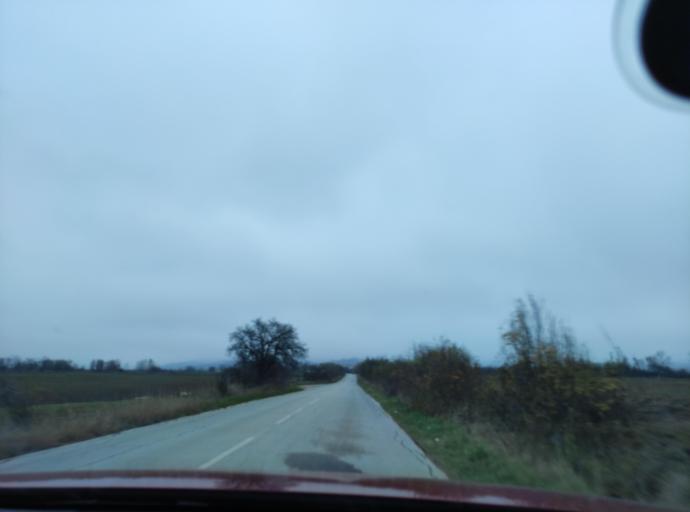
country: BG
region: Lovech
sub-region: Obshtina Yablanitsa
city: Yablanitsa
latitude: 43.0797
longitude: 24.0777
